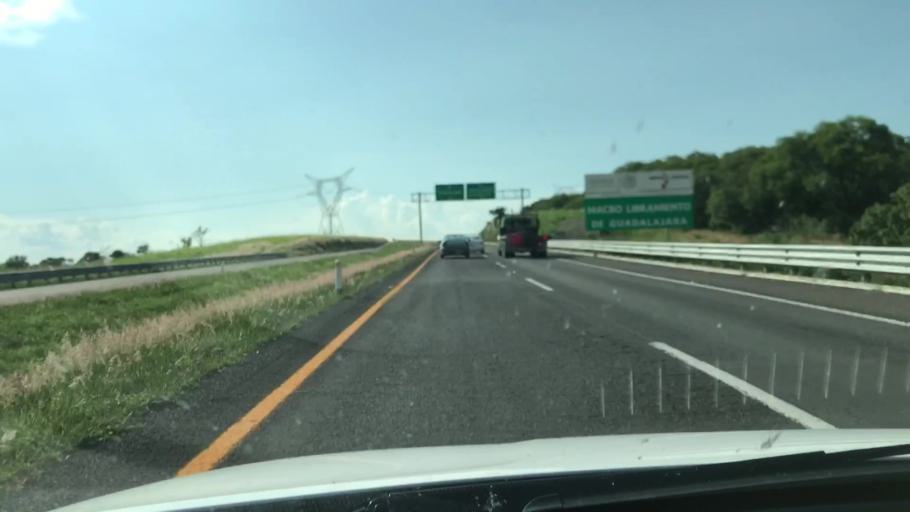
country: MX
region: Jalisco
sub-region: Zapotlanejo
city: La Mezquitera
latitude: 20.5794
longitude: -103.0915
